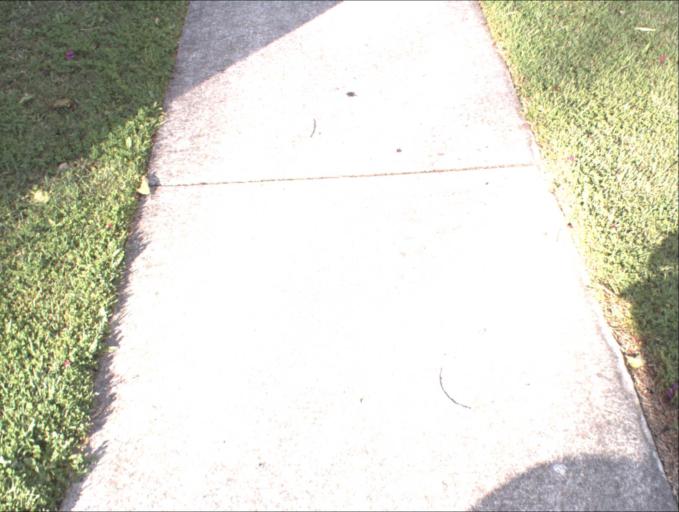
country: AU
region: Queensland
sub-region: Logan
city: Beenleigh
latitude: -27.7054
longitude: 153.1741
